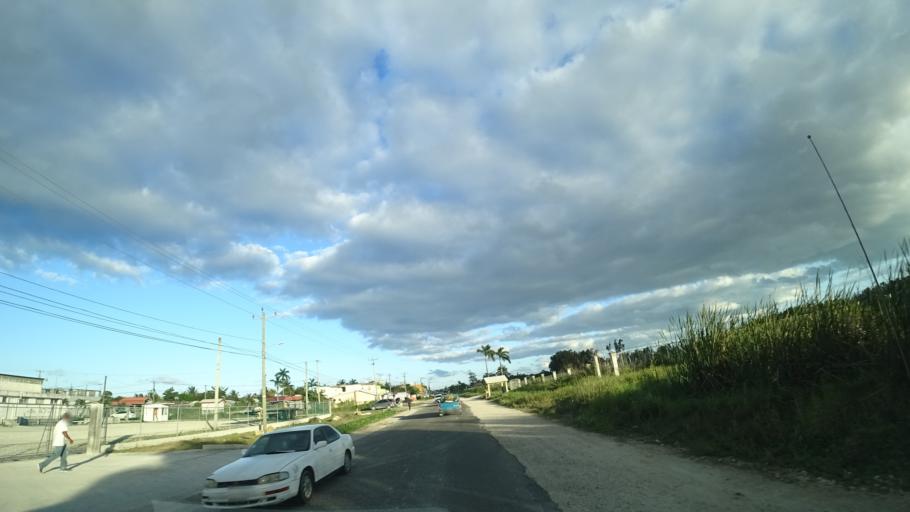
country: BZ
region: Belize
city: Belize City
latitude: 17.5473
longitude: -88.2943
